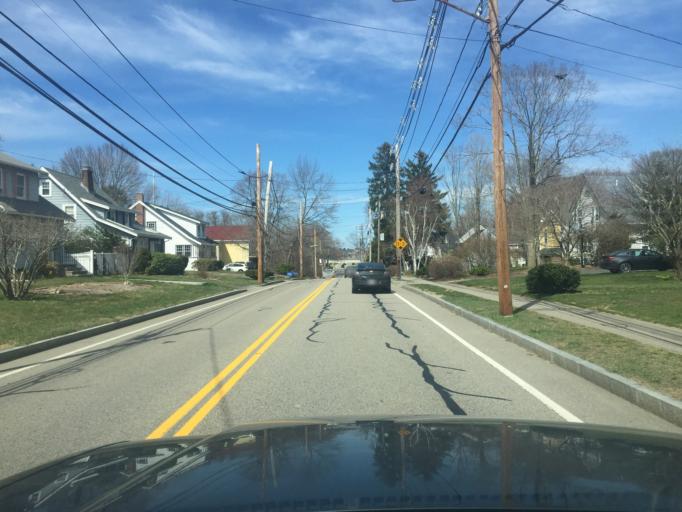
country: US
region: Massachusetts
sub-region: Norfolk County
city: Needham
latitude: 42.2705
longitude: -71.2384
